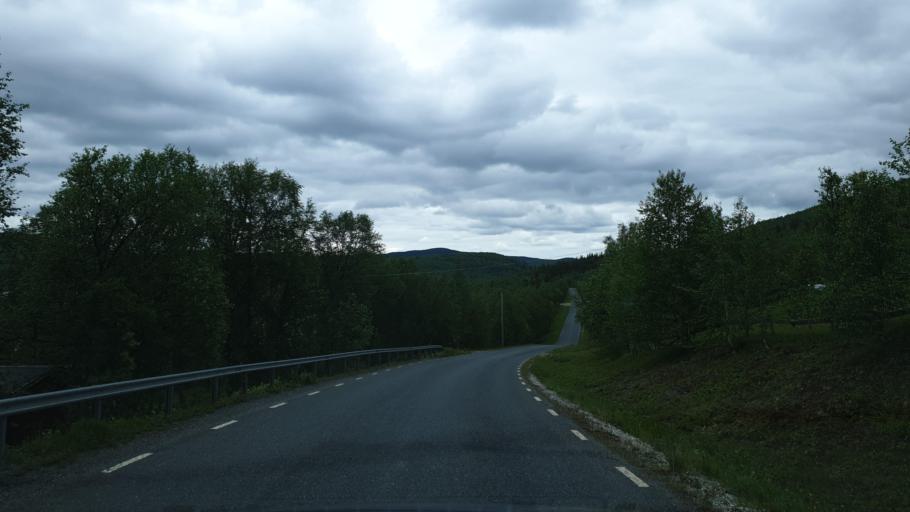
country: SE
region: Vaesterbotten
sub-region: Vilhelmina Kommun
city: Sjoberg
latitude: 65.2861
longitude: 15.2940
